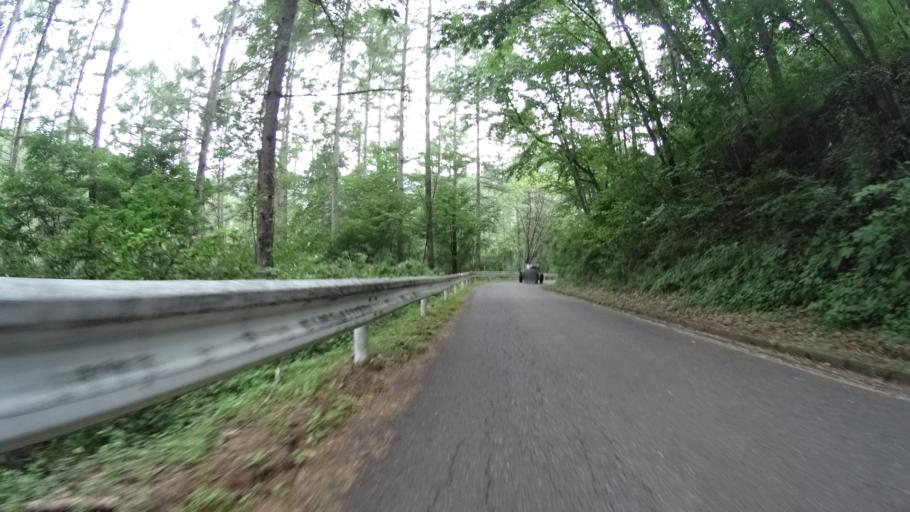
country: JP
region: Nagano
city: Saku
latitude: 36.0698
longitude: 138.6296
